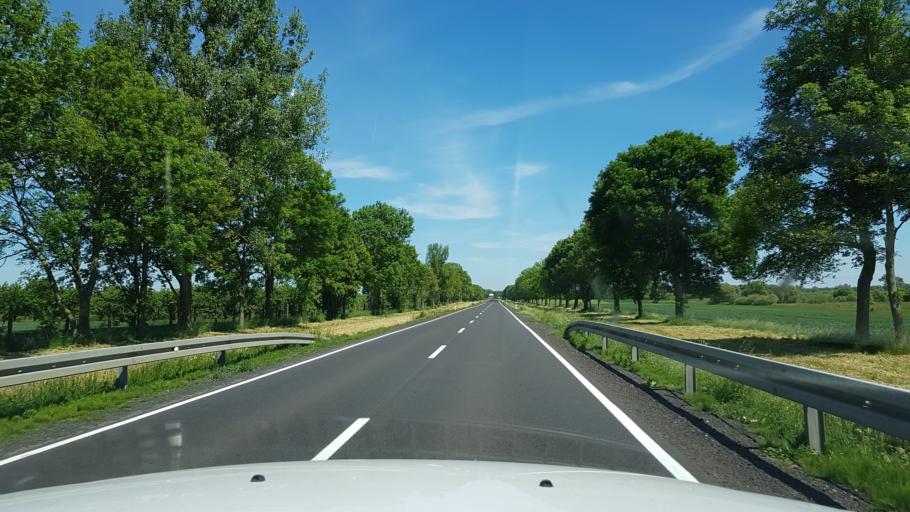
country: PL
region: West Pomeranian Voivodeship
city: Trzcinsko Zdroj
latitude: 52.9615
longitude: 14.5790
